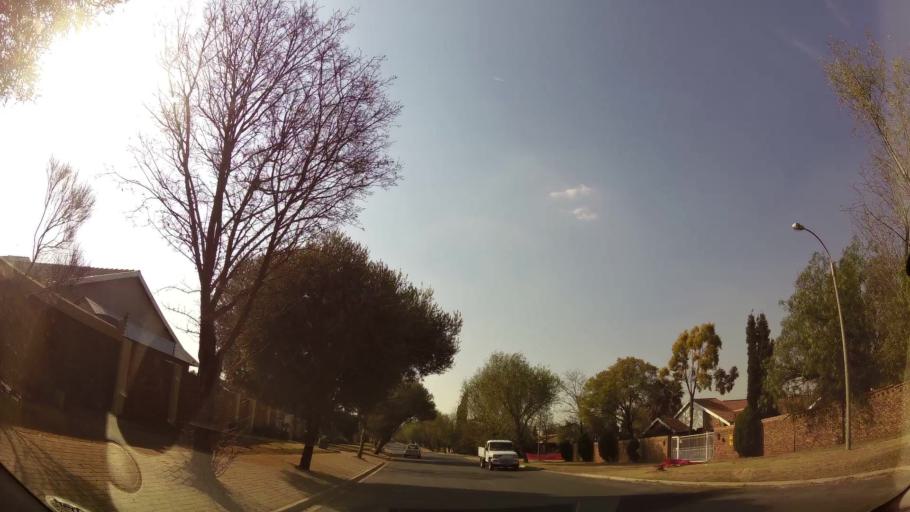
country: ZA
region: Gauteng
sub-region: Ekurhuleni Metropolitan Municipality
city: Benoni
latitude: -26.1575
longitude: 28.2820
